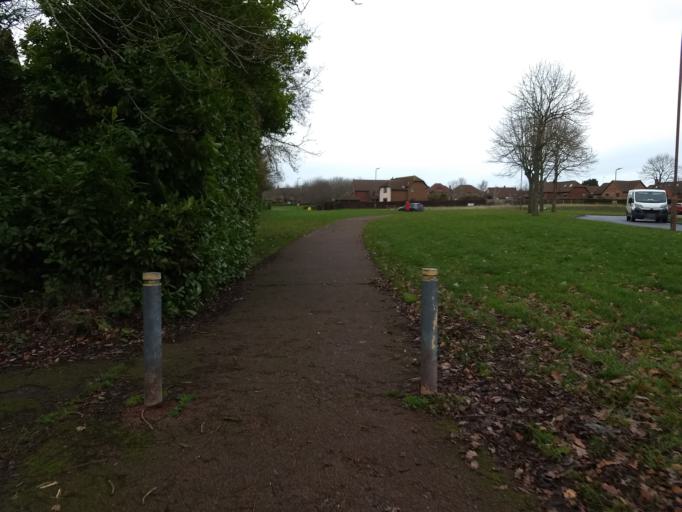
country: GB
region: England
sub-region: Buckinghamshire
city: Newton Longville
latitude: 51.9861
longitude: -0.7709
